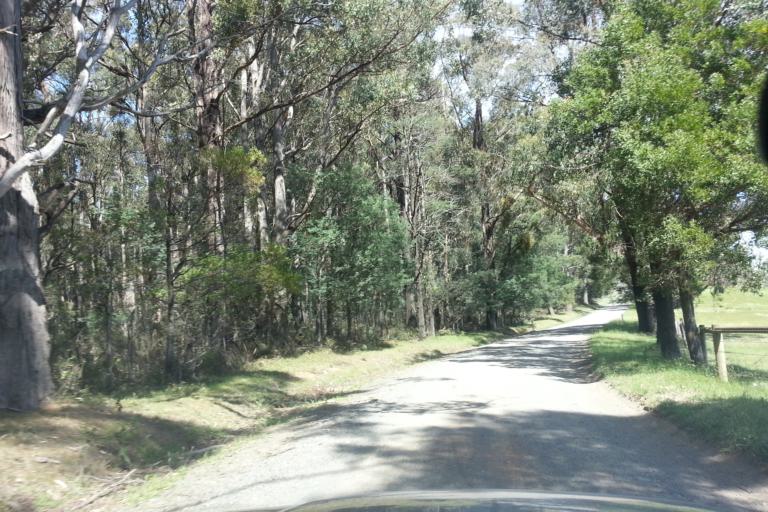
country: AU
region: Victoria
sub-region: Cardinia
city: Gembrook
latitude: -37.9358
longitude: 145.5827
